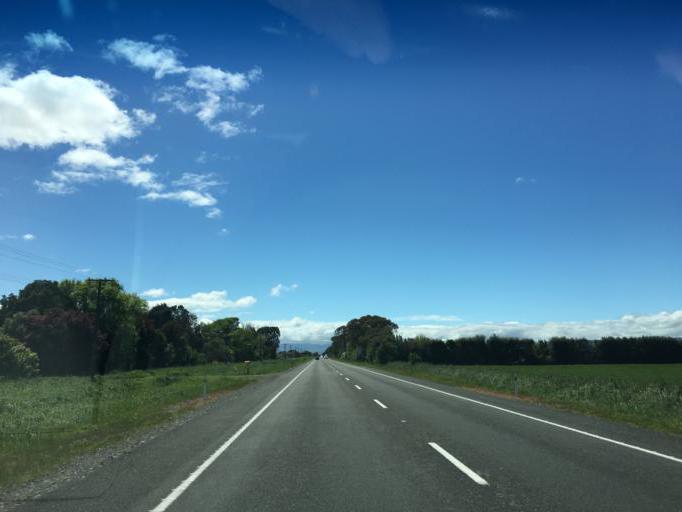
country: NZ
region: Manawatu-Wanganui
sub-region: Palmerston North City
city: Palmerston North
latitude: -40.3970
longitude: 175.5132
